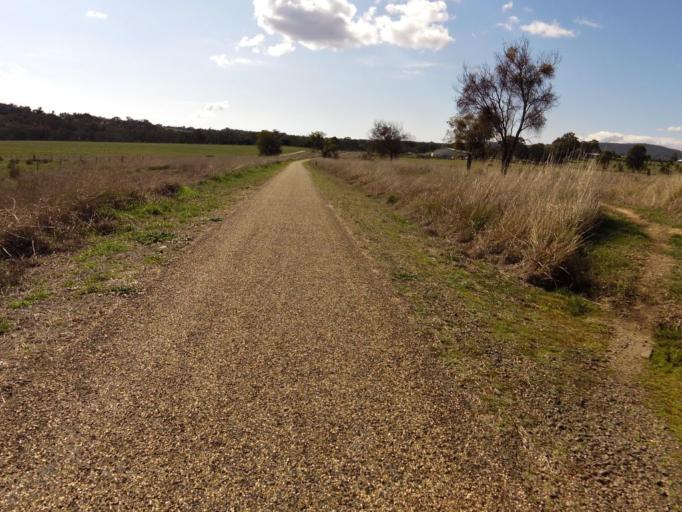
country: AU
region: Victoria
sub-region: Wangaratta
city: Wangaratta
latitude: -36.3968
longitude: 146.6531
